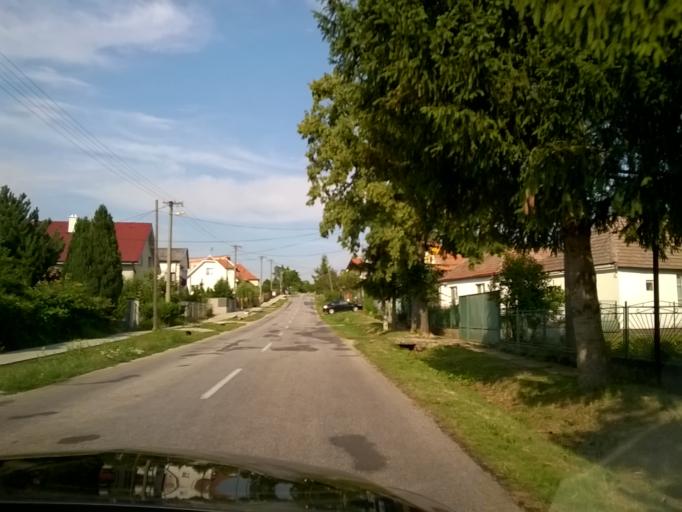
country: SK
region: Nitriansky
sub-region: Okres Nitra
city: Nitra
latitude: 48.3651
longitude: 17.9572
